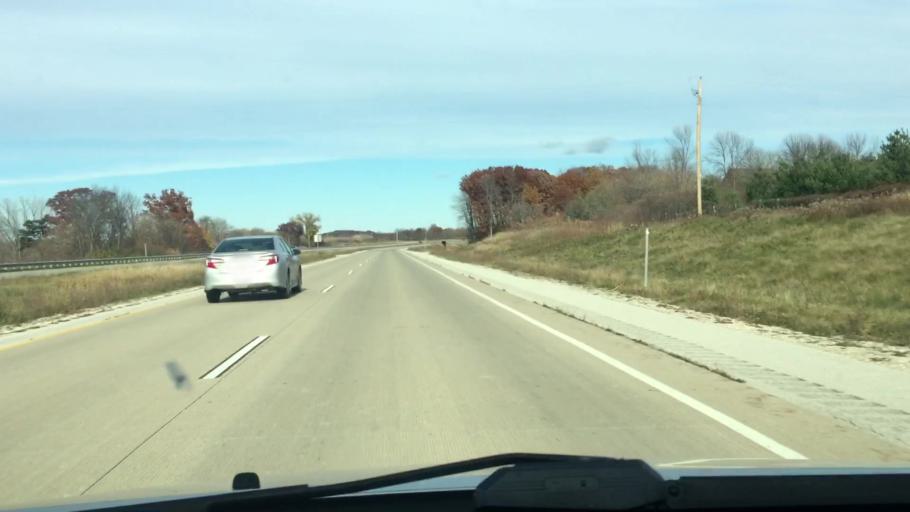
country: US
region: Wisconsin
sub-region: Kewaunee County
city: Luxemburg
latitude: 44.7003
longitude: -87.7098
